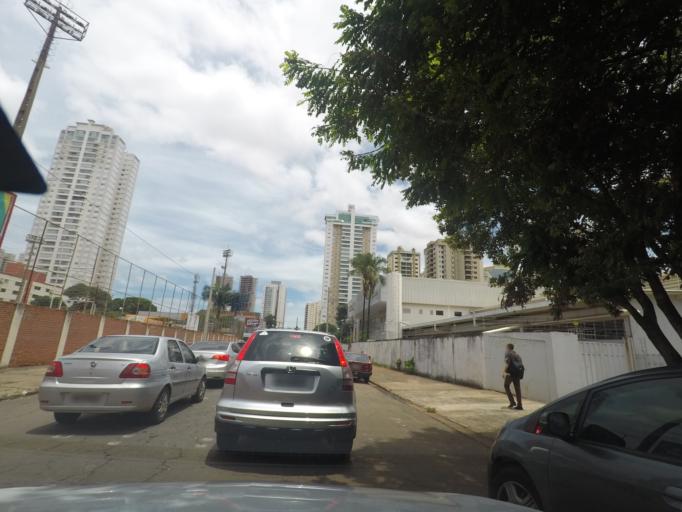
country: BR
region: Goias
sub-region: Goiania
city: Goiania
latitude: -16.6942
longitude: -49.2756
